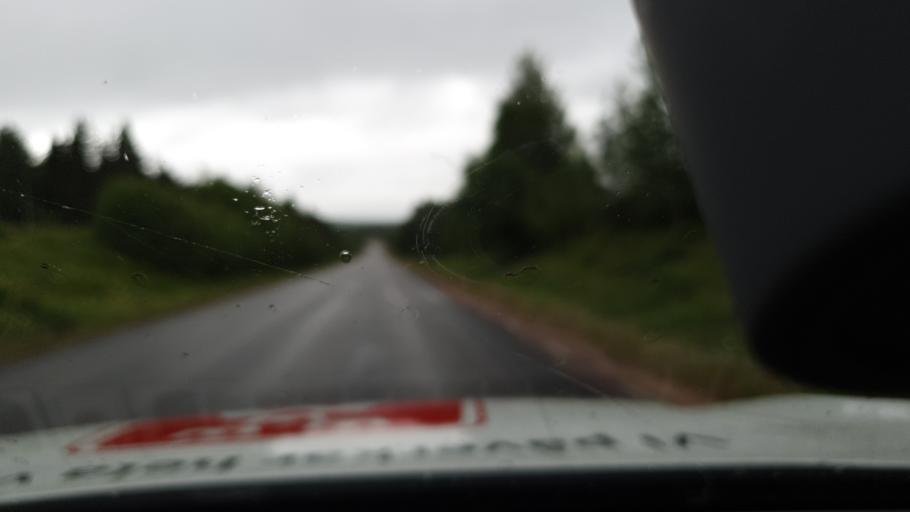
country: SE
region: Norrbotten
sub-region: Overtornea Kommun
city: OEvertornea
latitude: 66.4519
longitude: 23.6212
